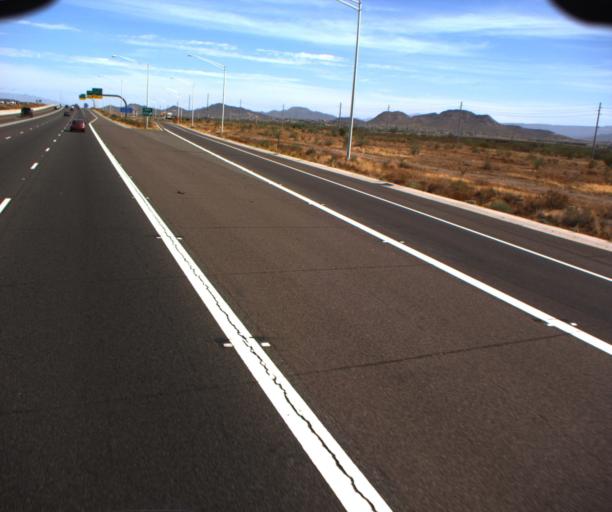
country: US
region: Arizona
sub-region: Maricopa County
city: Anthem
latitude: 33.7635
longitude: -112.1279
